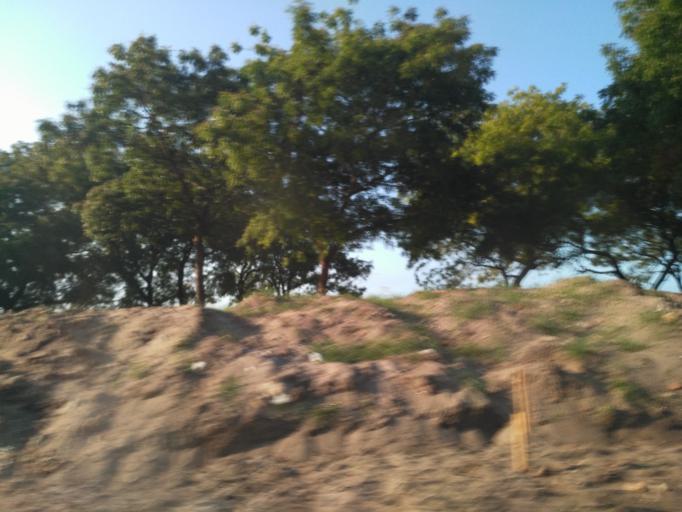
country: TZ
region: Dar es Salaam
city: Magomeni
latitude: -6.7609
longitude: 39.2623
